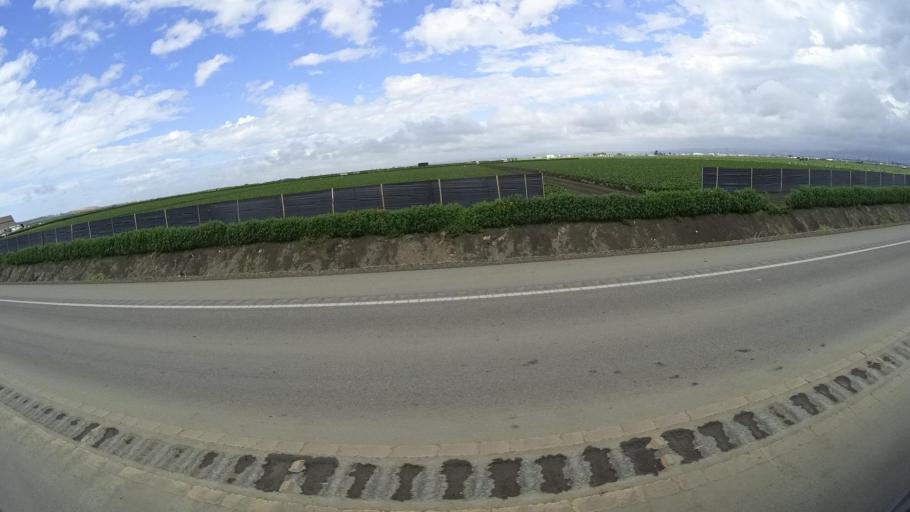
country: US
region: California
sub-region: Monterey County
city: Boronda
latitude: 36.6777
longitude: -121.7117
